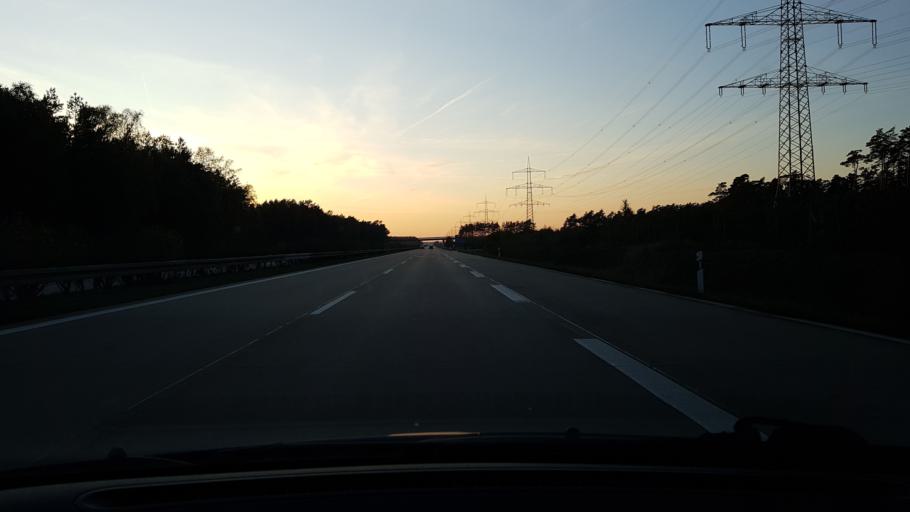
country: DE
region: Mecklenburg-Vorpommern
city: Zarrentin
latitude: 53.5113
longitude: 10.9012
